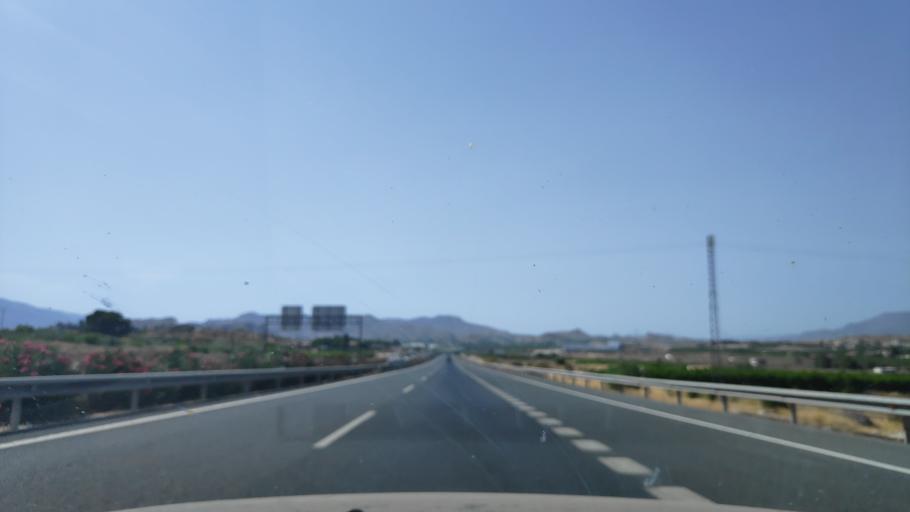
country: ES
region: Murcia
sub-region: Murcia
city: Archena
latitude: 38.1265
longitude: -1.2575
